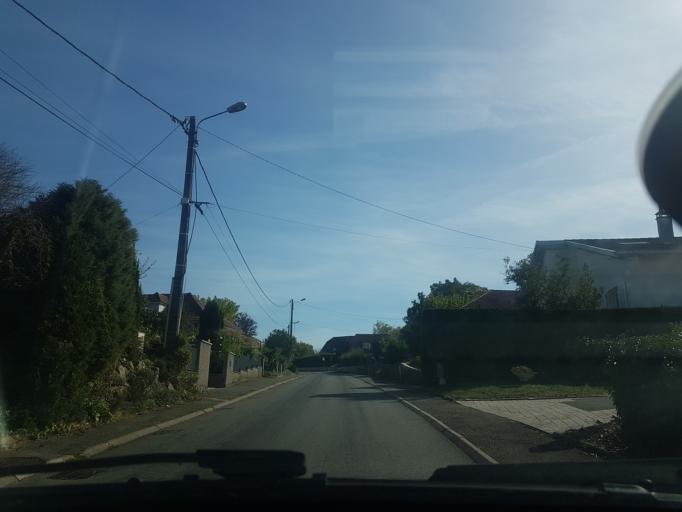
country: FR
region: Franche-Comte
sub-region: Territoire de Belfort
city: Chevremont
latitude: 47.6586
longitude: 6.9180
